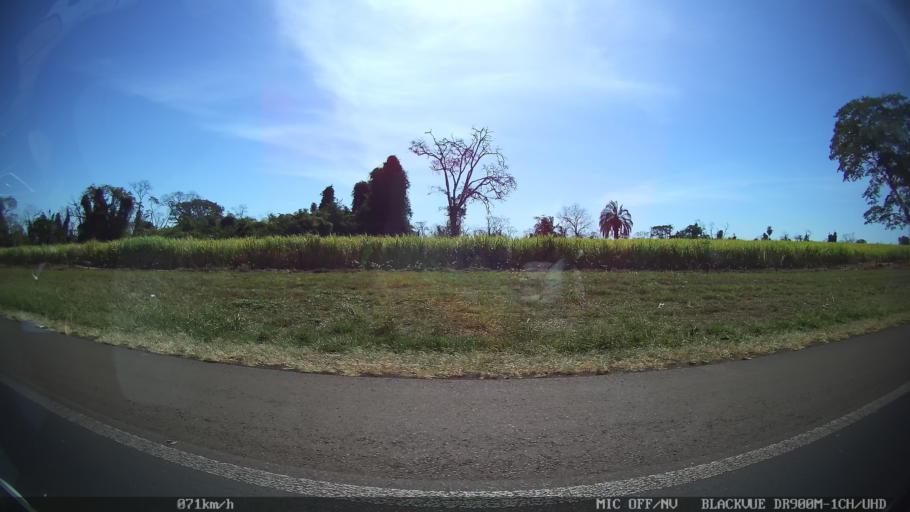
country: BR
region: Sao Paulo
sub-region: Barretos
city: Barretos
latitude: -20.5735
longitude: -48.6760
